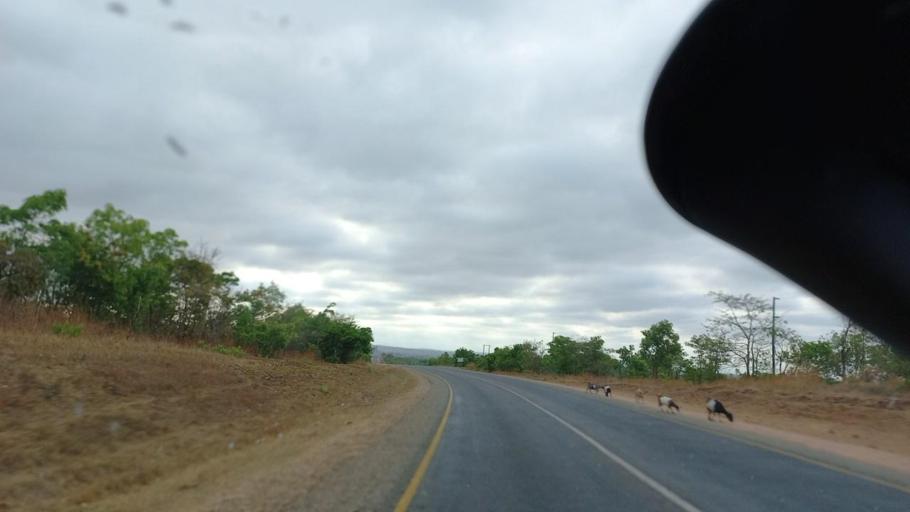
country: ZM
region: Lusaka
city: Chongwe
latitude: -15.2773
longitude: 28.7721
